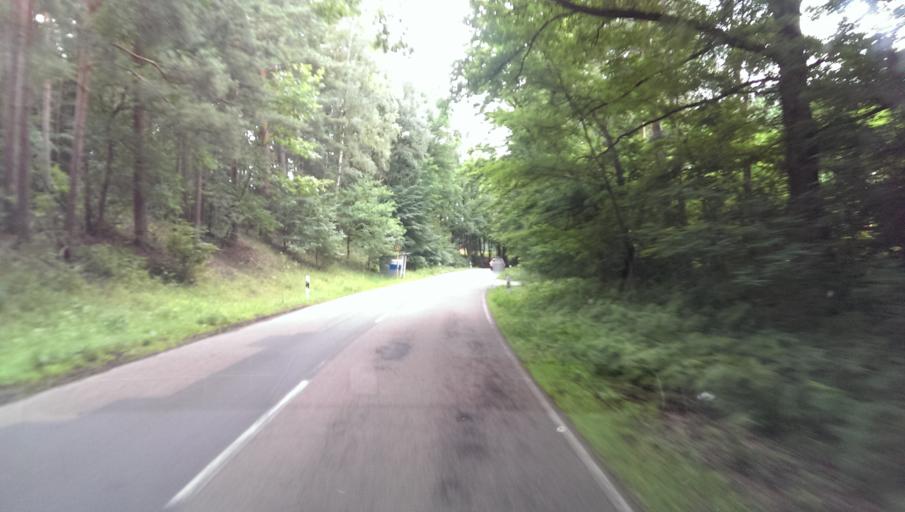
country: DE
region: Saxony-Anhalt
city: Nudersdorf
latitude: 51.9212
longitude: 12.5407
